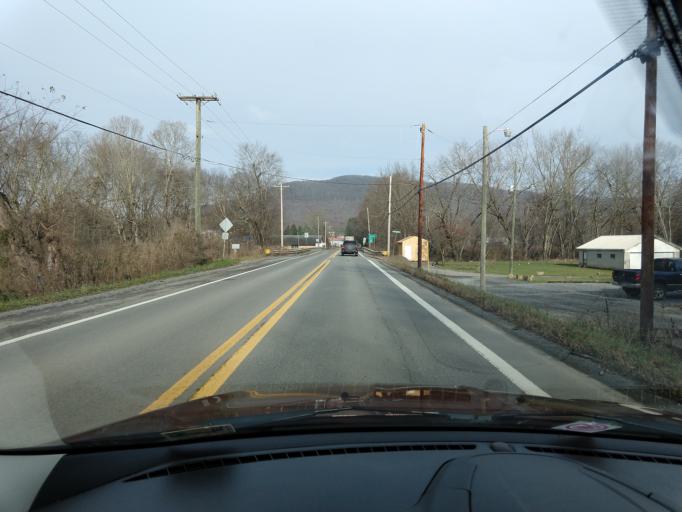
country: US
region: West Virginia
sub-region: Greenbrier County
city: Rainelle
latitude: 37.9576
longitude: -80.6830
